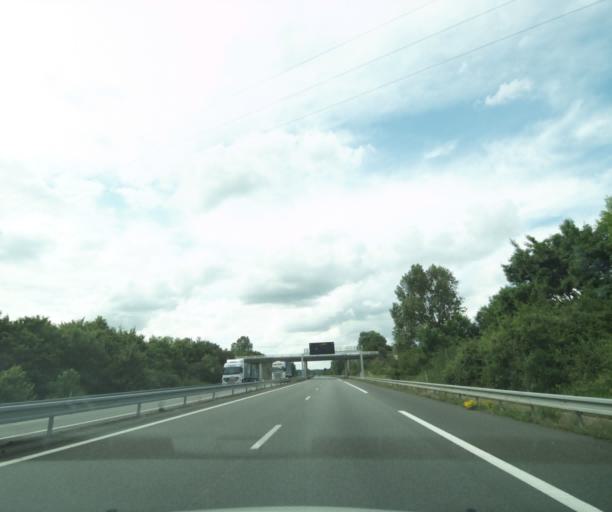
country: FR
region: Centre
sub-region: Departement du Cher
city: Foecy
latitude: 47.1858
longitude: 2.1691
